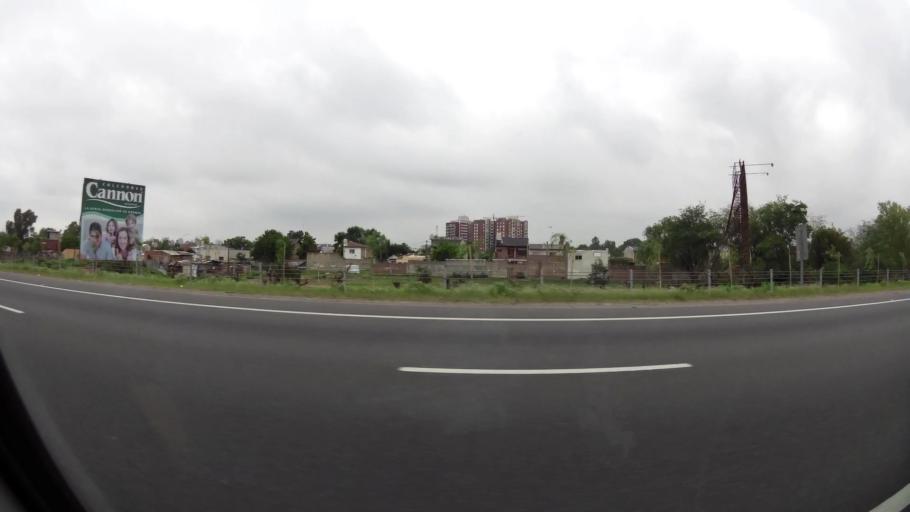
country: AR
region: Buenos Aires
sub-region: Partido de Quilmes
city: Quilmes
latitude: -34.7056
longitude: -58.2666
